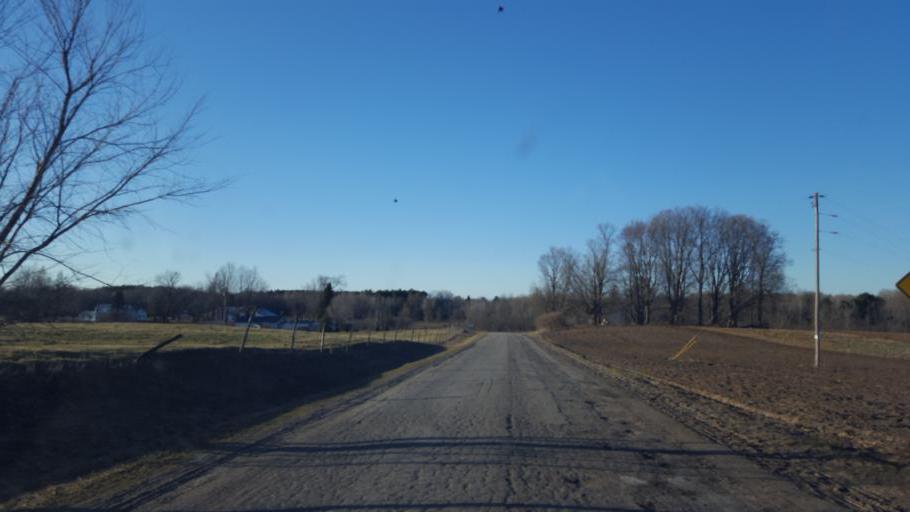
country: US
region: Michigan
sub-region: Mecosta County
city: Canadian Lakes
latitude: 43.5527
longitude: -85.3929
